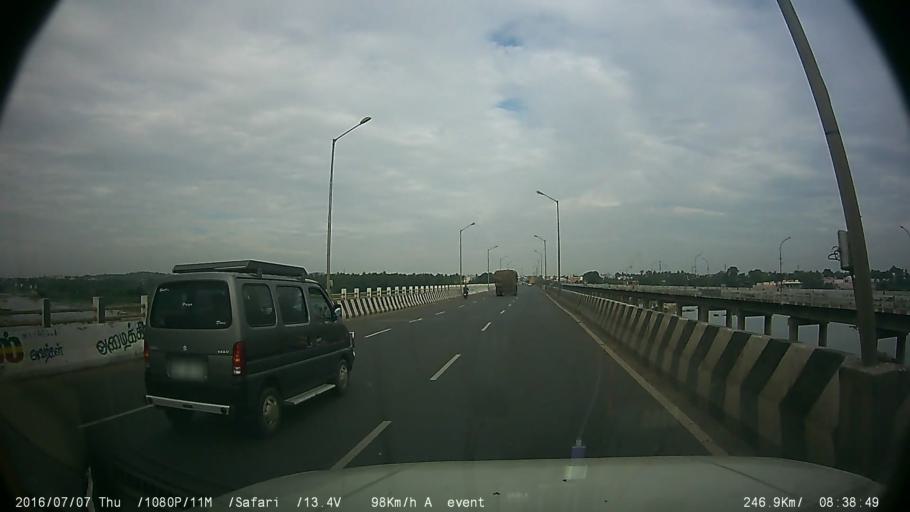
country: IN
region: Tamil Nadu
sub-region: Erode
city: Bhavani
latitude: 11.4307
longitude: 77.6880
